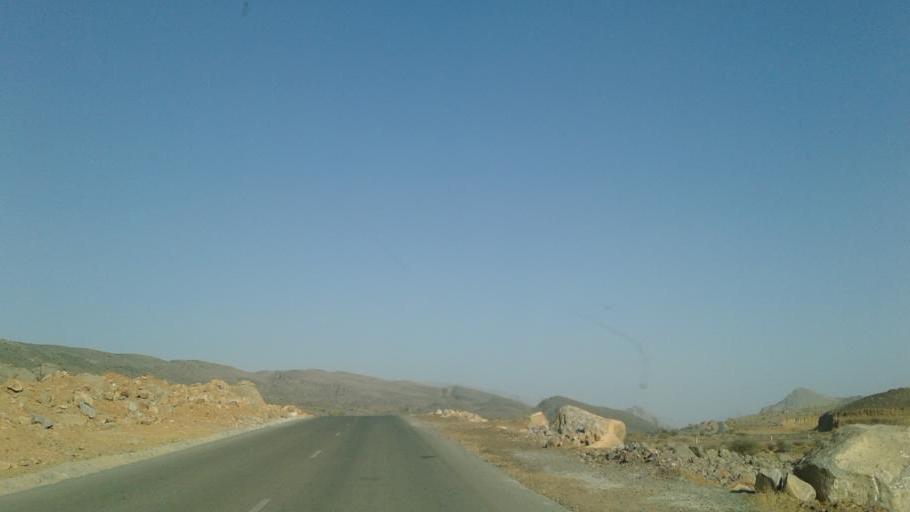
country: OM
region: Muhafazat ad Dakhiliyah
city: Bahla'
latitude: 23.0780
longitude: 57.3500
